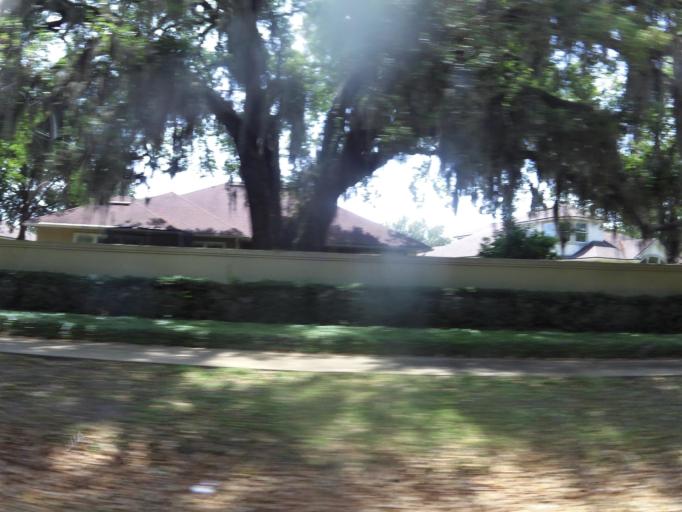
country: US
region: Florida
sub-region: Duval County
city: Jacksonville
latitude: 30.4590
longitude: -81.5308
